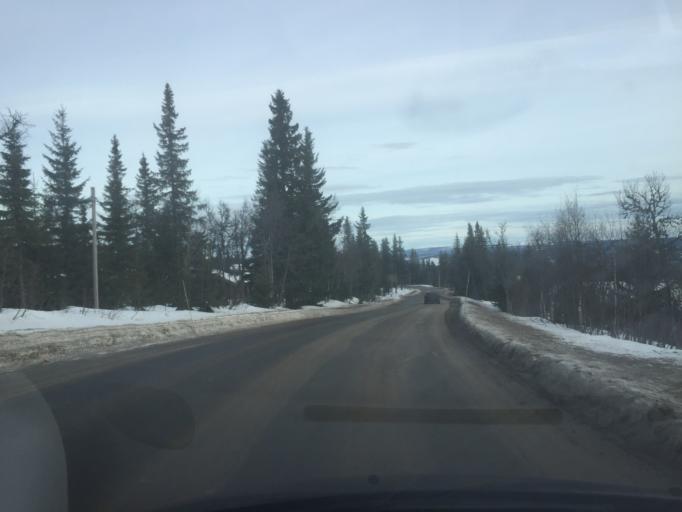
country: NO
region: Hedmark
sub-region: Trysil
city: Innbygda
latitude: 61.3312
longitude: 12.1627
